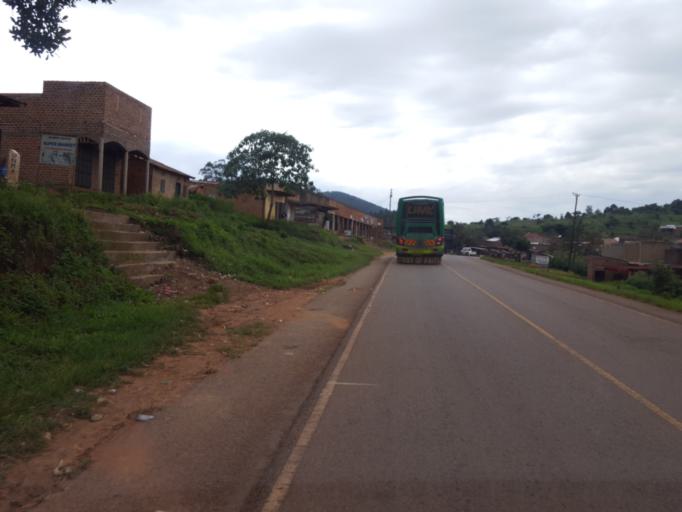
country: UG
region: Central Region
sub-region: Mityana District
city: Mityana
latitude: 0.6725
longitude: 32.0850
